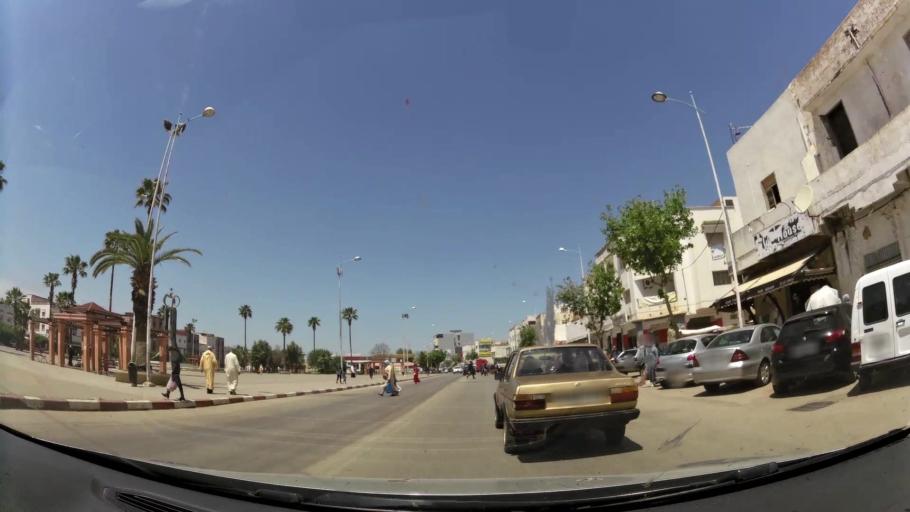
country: MA
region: Rabat-Sale-Zemmour-Zaer
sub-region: Khemisset
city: Khemisset
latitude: 33.8256
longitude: -6.0683
